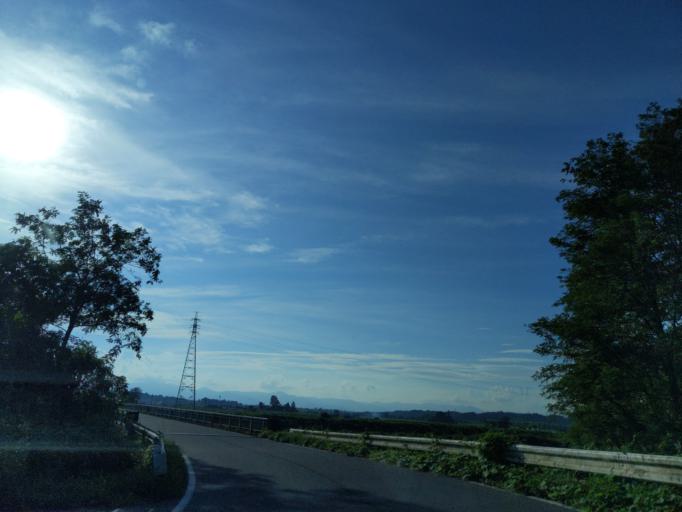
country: JP
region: Fukushima
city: Sukagawa
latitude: 37.2872
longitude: 140.4140
